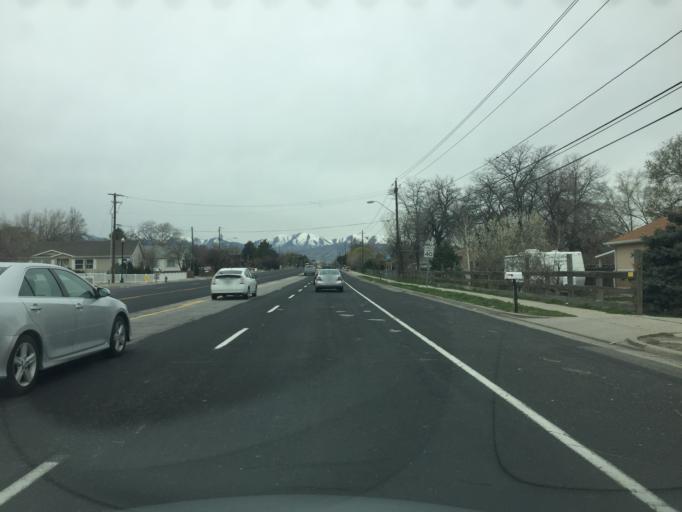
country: US
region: Utah
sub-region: Salt Lake County
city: Kearns
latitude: 40.6676
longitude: -111.9712
